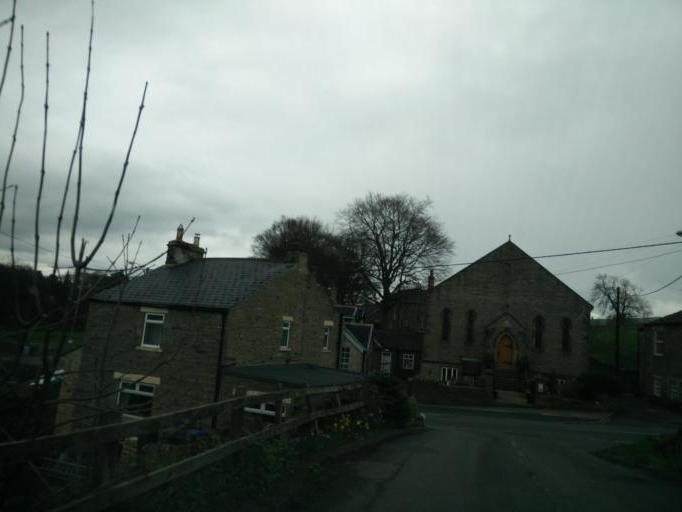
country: GB
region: England
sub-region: County Durham
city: Stanhope
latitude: 54.7256
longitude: -1.9673
